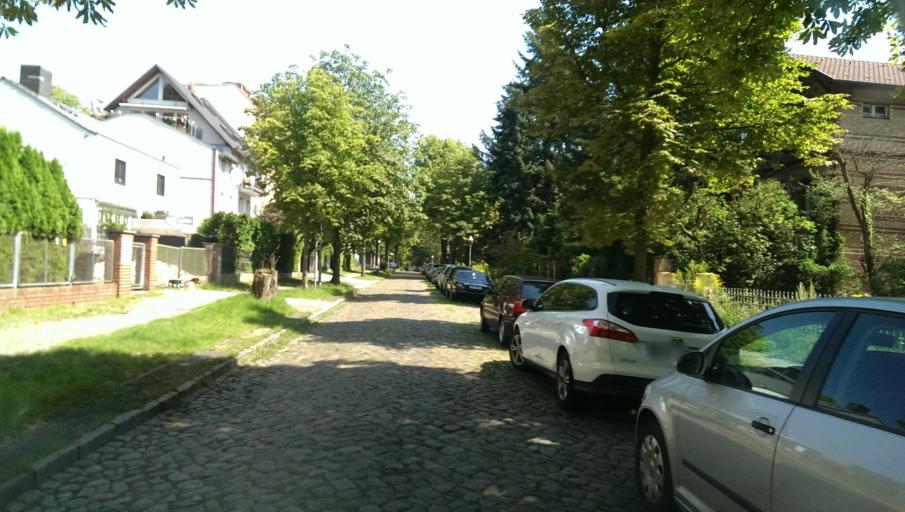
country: DE
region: Berlin
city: Lichterfelde
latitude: 52.4437
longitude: 13.3022
